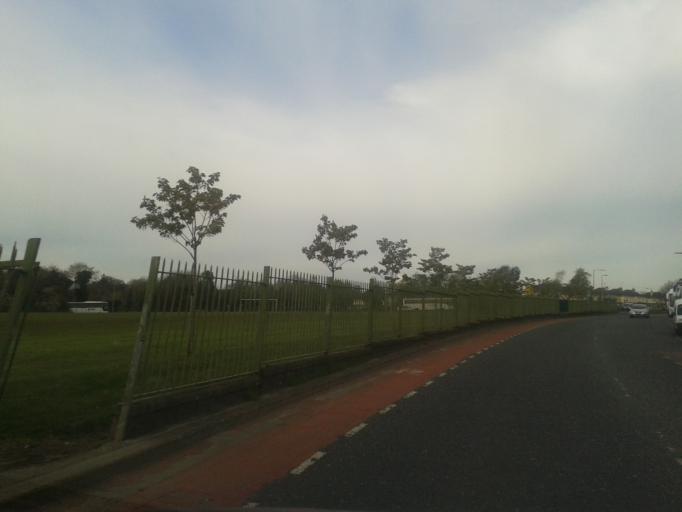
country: IE
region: Leinster
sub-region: Fingal County
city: Swords
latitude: 53.4596
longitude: -6.2501
